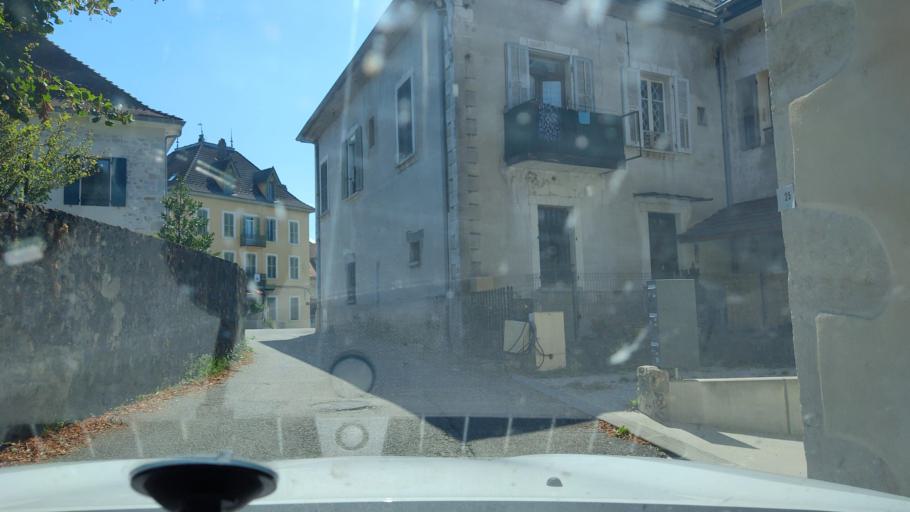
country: FR
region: Rhone-Alpes
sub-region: Departement de la Savoie
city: Novalaise
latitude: 45.5953
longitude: 5.7702
